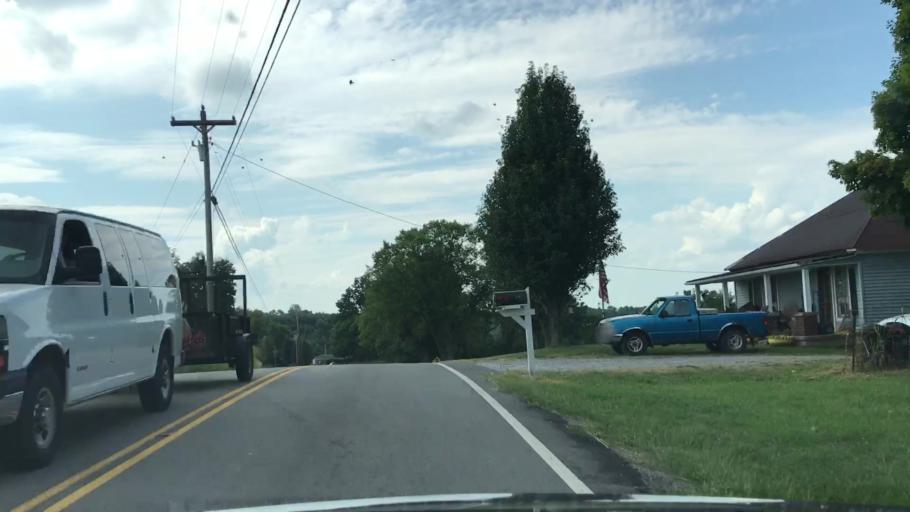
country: US
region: Tennessee
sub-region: Sumner County
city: Westmoreland
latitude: 36.5166
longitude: -86.1793
